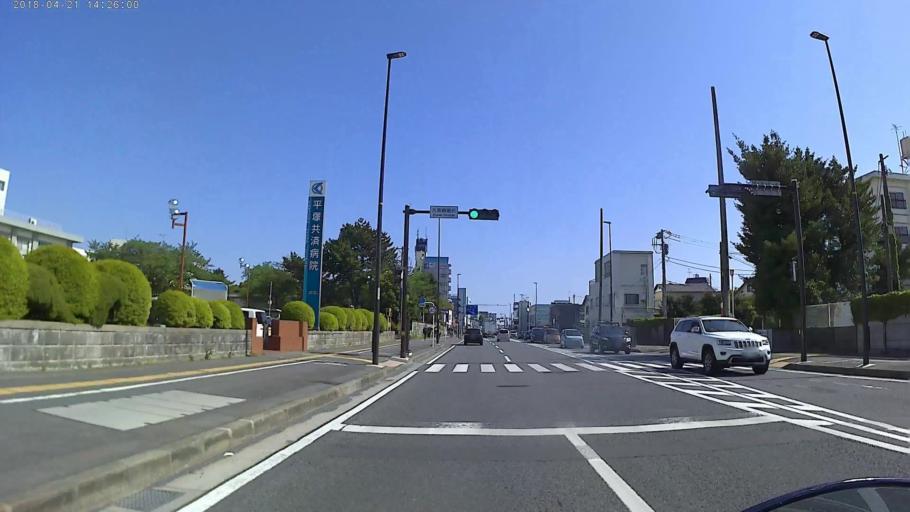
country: JP
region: Kanagawa
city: Hiratsuka
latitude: 35.3384
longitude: 139.3371
